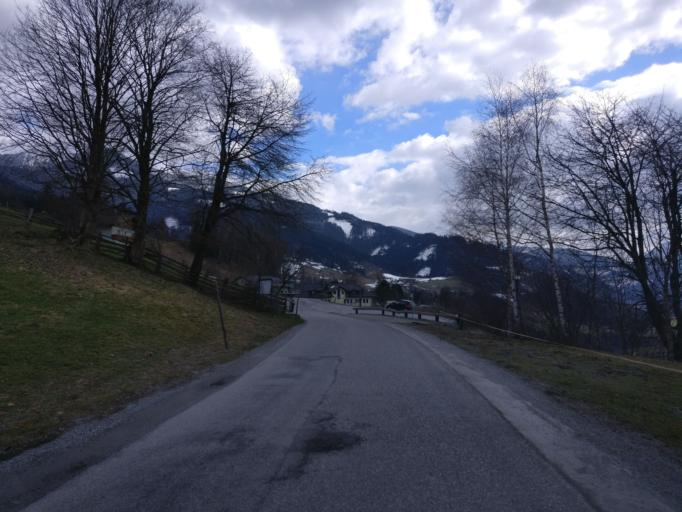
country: AT
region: Salzburg
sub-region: Politischer Bezirk Sankt Johann im Pongau
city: Bischofshofen
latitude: 47.4090
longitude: 13.2284
